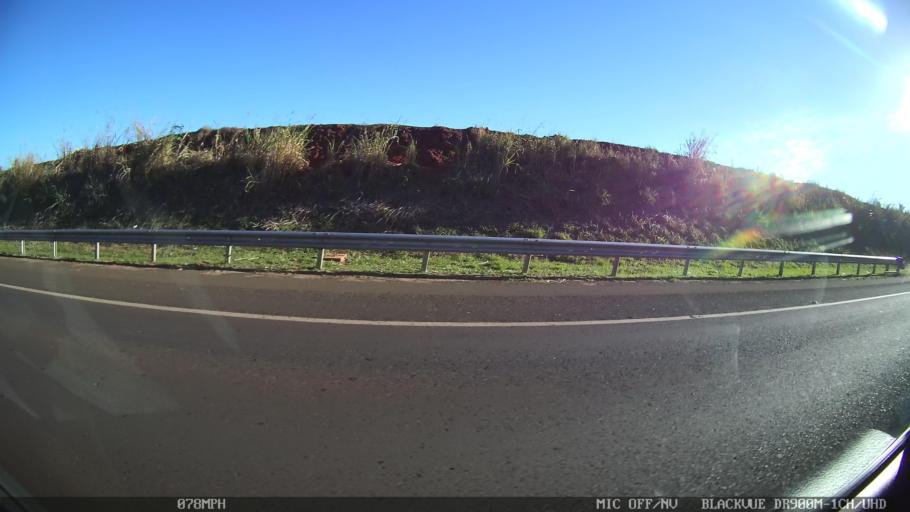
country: BR
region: Sao Paulo
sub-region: Americo Brasiliense
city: Americo Brasiliense
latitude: -21.7641
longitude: -48.1125
